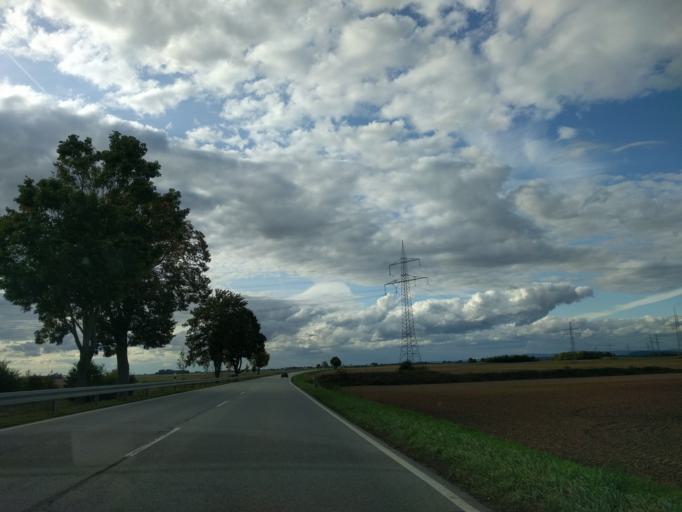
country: DE
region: Bavaria
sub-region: Lower Bavaria
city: Stephansposching
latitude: 48.8122
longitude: 12.7694
